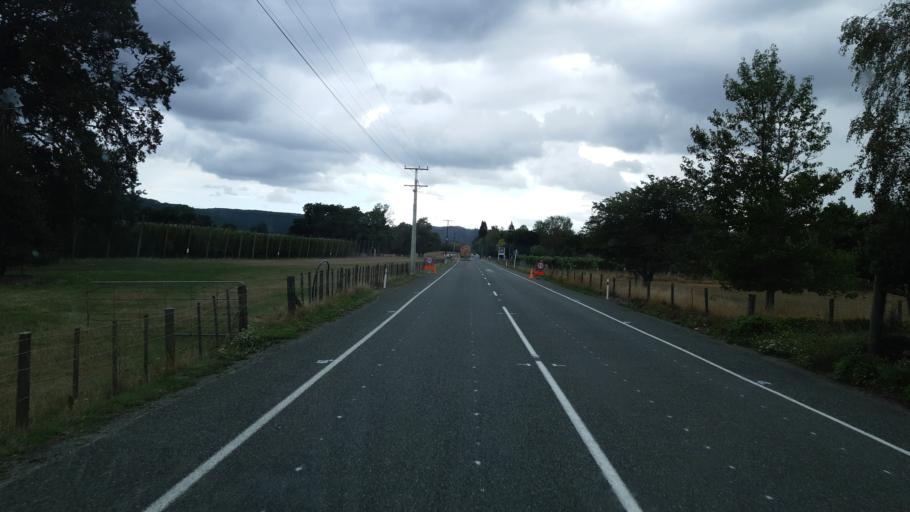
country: NZ
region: Tasman
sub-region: Tasman District
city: Wakefield
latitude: -41.4195
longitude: 173.0073
